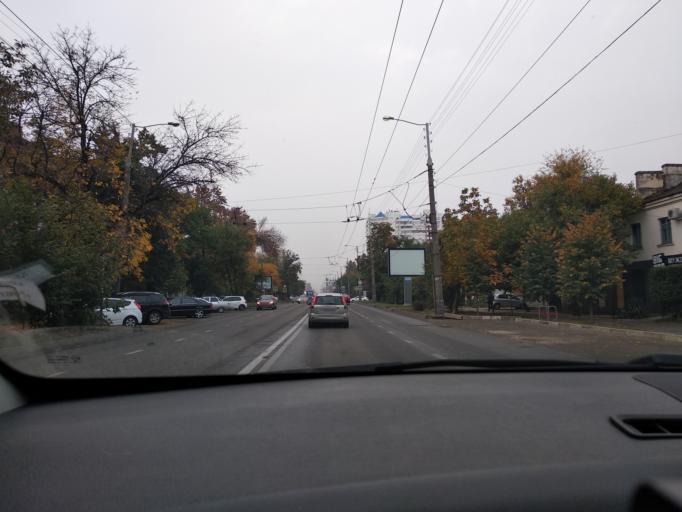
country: RU
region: Krasnodarskiy
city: Krasnodar
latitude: 45.0556
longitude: 38.9605
